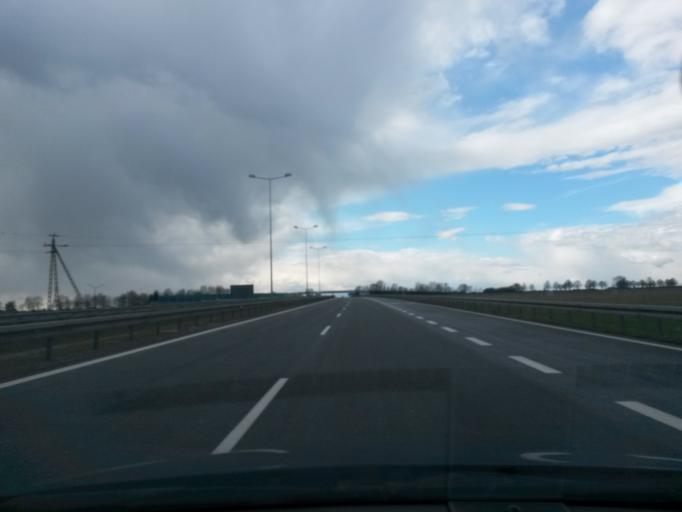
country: PL
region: Greater Poland Voivodeship
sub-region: Powiat koninski
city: Rzgow Pierwszy
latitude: 52.2061
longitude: 18.0176
